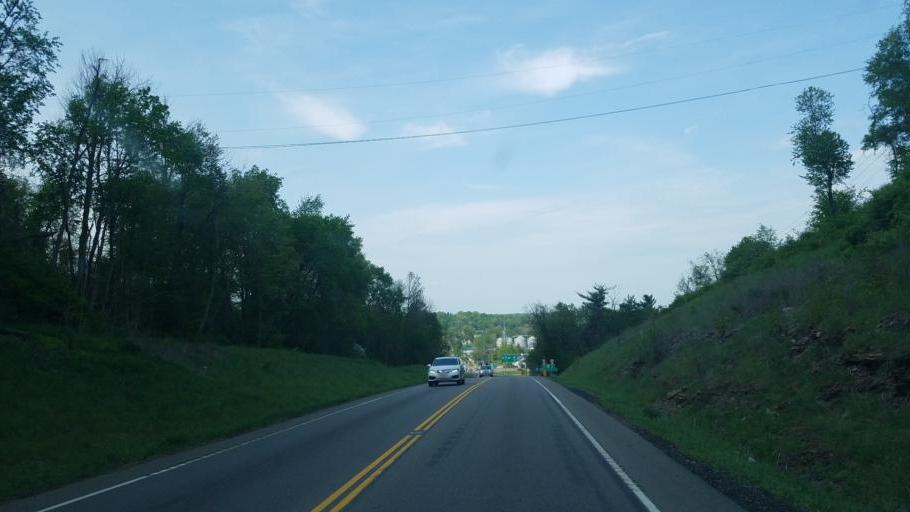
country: US
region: Ohio
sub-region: Licking County
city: Granville
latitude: 40.0549
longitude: -82.5218
